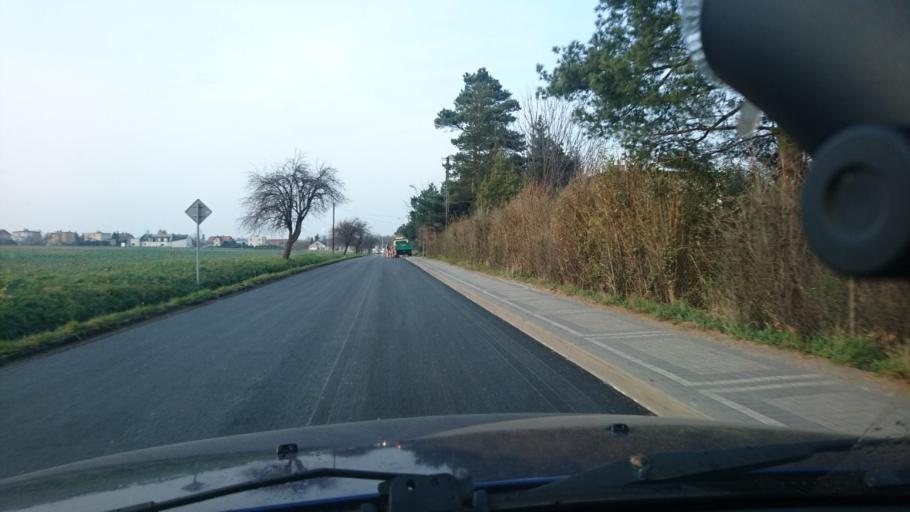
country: PL
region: Silesian Voivodeship
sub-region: Powiat bielski
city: Jaworze
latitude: 49.8024
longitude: 18.9426
